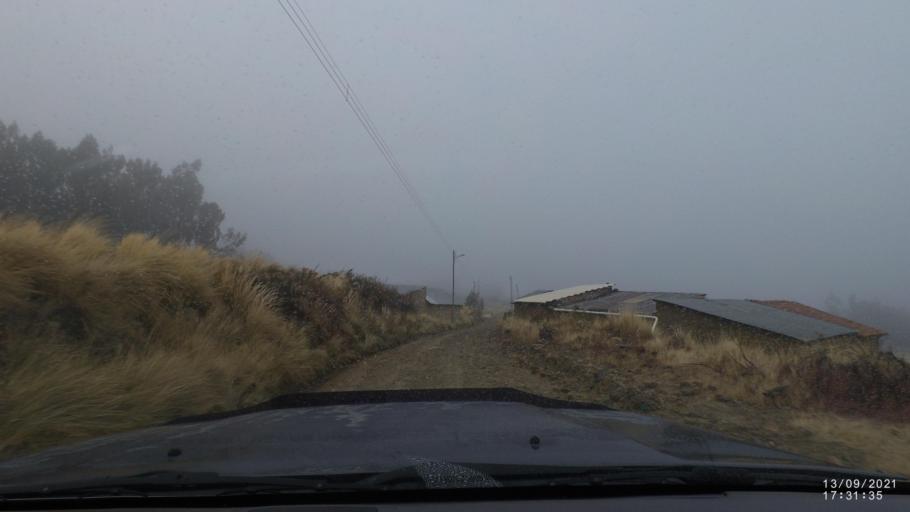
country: BO
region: Cochabamba
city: Colomi
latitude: -17.3636
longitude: -65.7873
